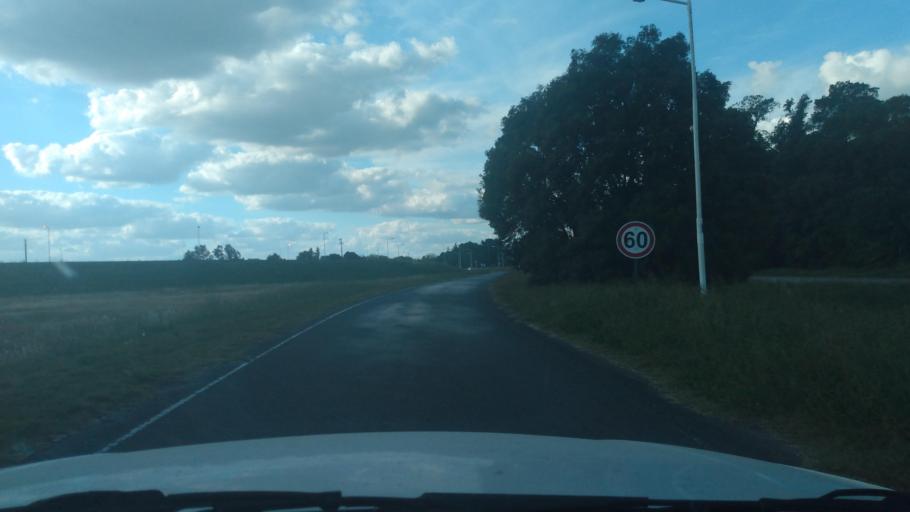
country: AR
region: Buenos Aires
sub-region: Partido de Mercedes
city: Mercedes
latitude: -34.6671
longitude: -59.3985
